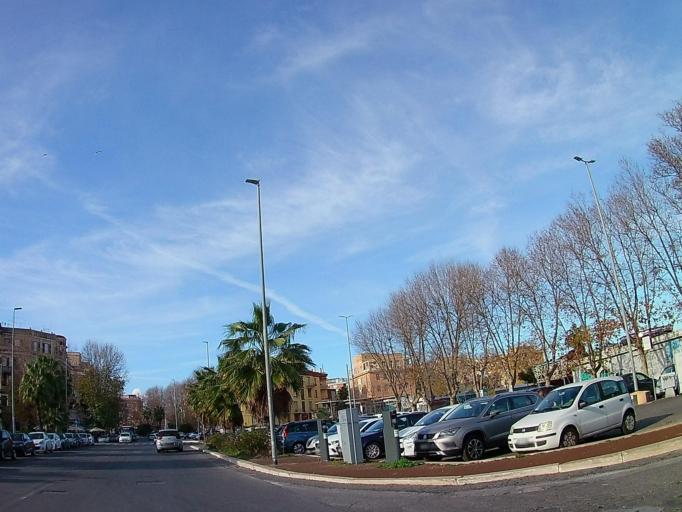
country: IT
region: Latium
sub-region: Citta metropolitana di Roma Capitale
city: Lido di Ostia
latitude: 41.7311
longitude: 12.2802
